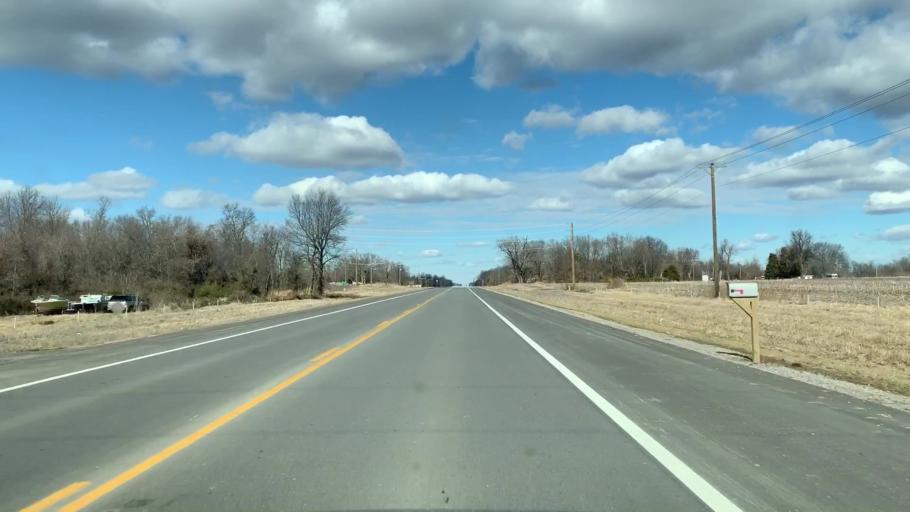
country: US
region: Kansas
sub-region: Cherokee County
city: Columbus
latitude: 37.2196
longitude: -94.8318
